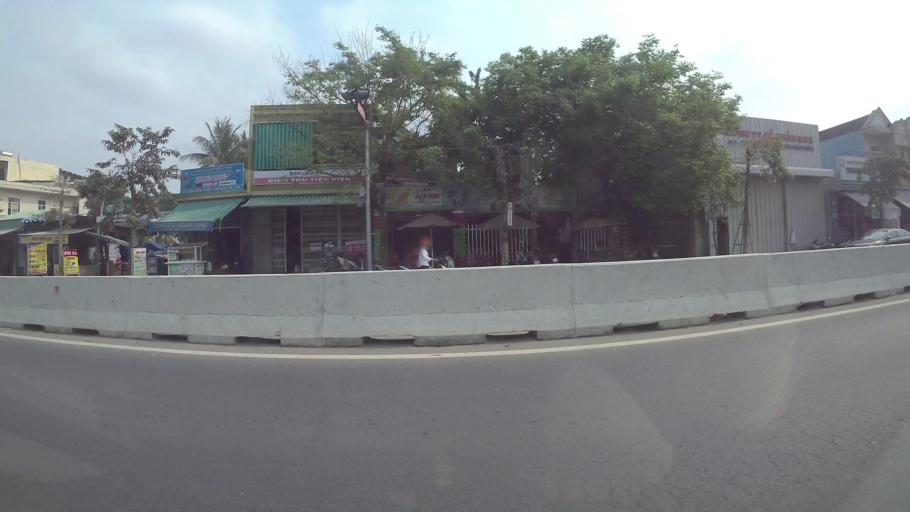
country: VN
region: Da Nang
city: Lien Chieu
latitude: 16.0533
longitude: 108.1557
